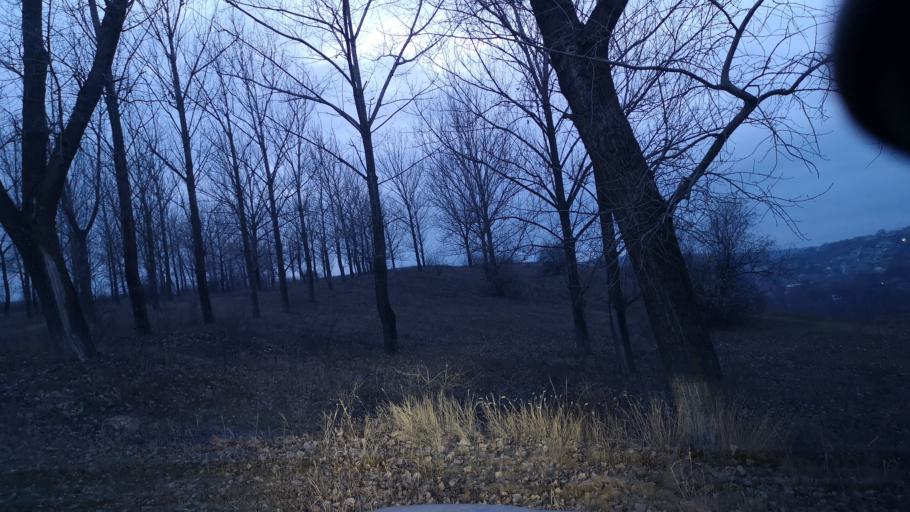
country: MD
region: Telenesti
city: Cocieri
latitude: 47.3076
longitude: 28.9877
